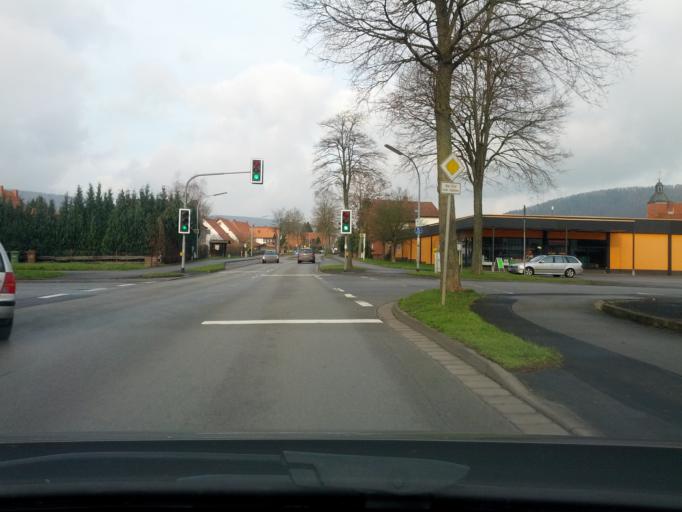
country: DE
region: Lower Saxony
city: Buhren
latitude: 51.4916
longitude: 9.6040
